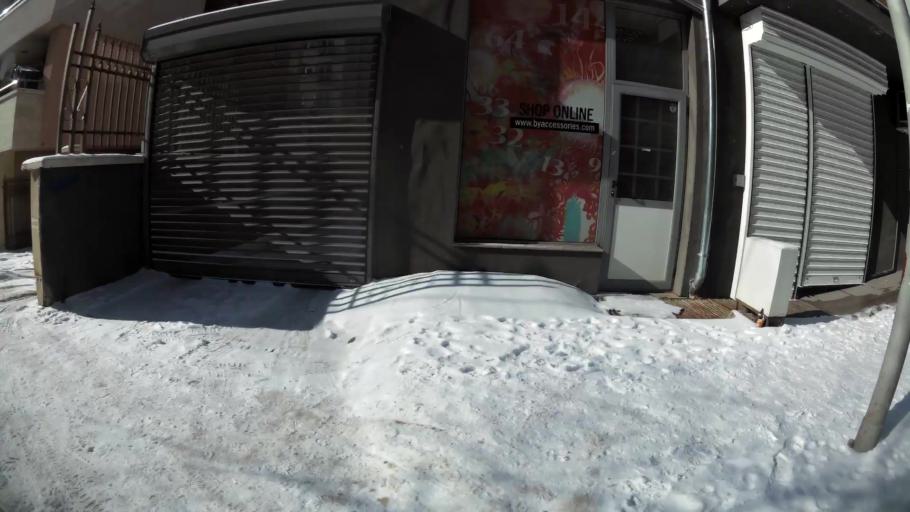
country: BG
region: Sofia-Capital
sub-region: Stolichna Obshtina
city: Sofia
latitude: 42.6613
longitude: 23.3158
